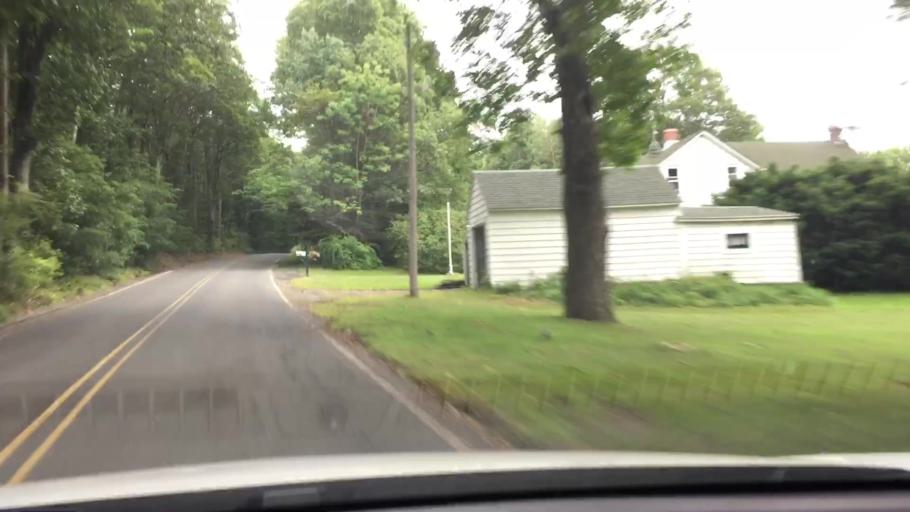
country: US
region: Massachusetts
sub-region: Berkshire County
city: Otis
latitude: 42.2459
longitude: -72.9876
